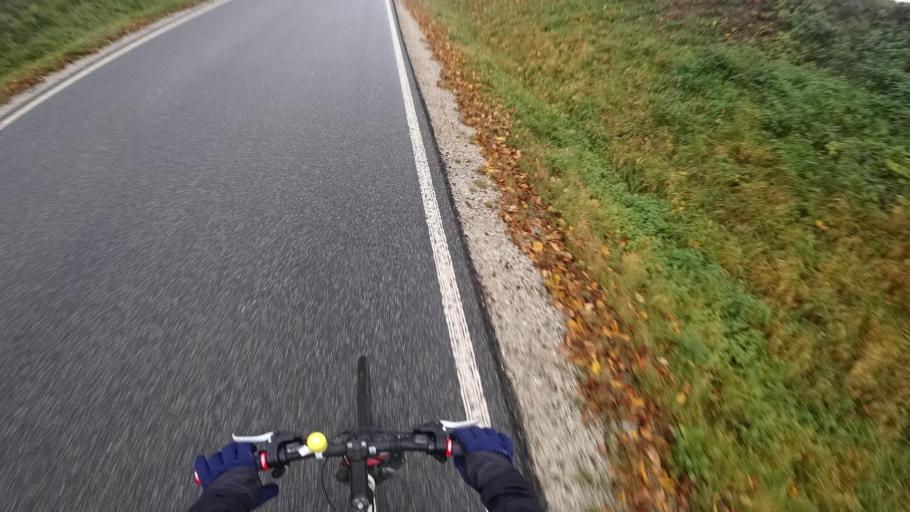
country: DE
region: Rheinland-Pfalz
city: Urbar
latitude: 50.1372
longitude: 7.7128
